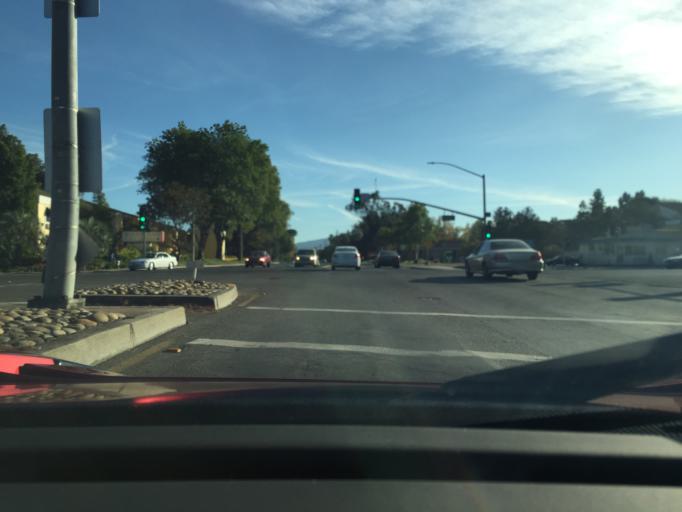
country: US
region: California
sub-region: Santa Clara County
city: Sunnyvale
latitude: 37.3525
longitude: -122.0142
